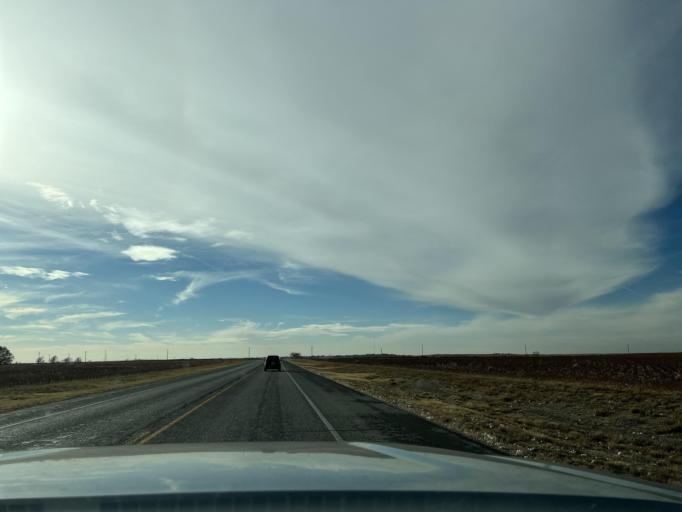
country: US
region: Texas
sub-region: Fisher County
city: Roby
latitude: 32.7522
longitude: -100.3437
